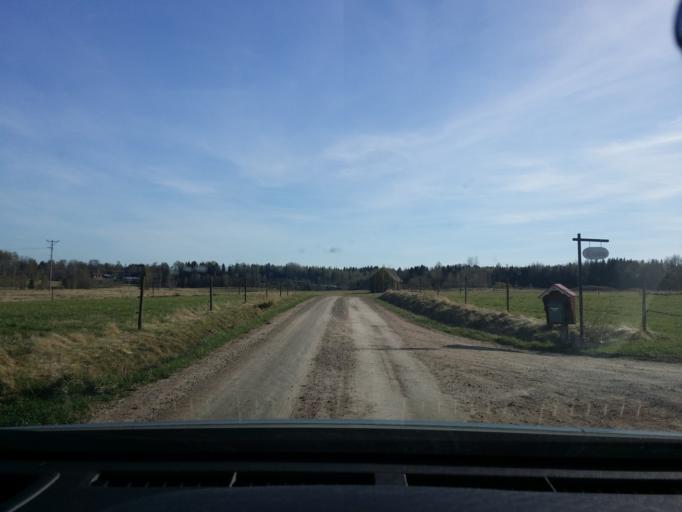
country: SE
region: Dalarna
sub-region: Avesta Kommun
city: Avesta
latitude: 60.0792
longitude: 16.3697
